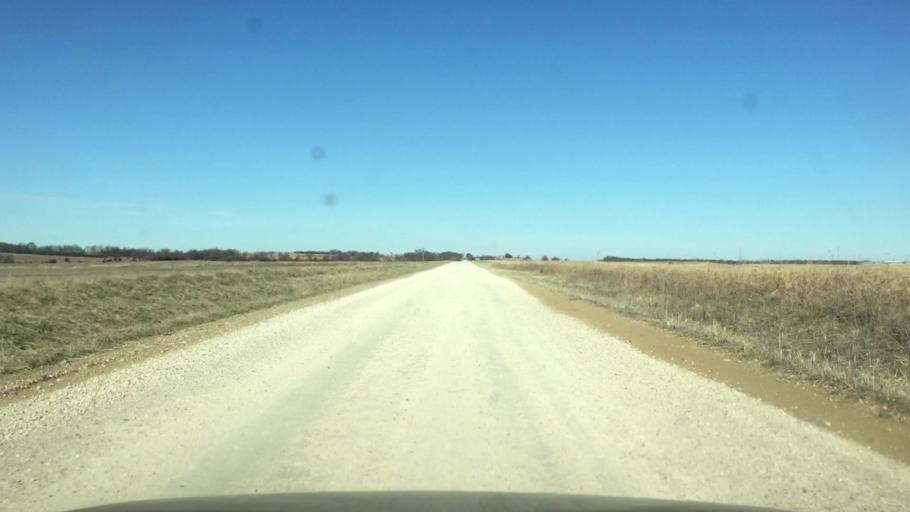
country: US
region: Kansas
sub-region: Allen County
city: Iola
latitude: 37.8596
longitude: -95.3910
